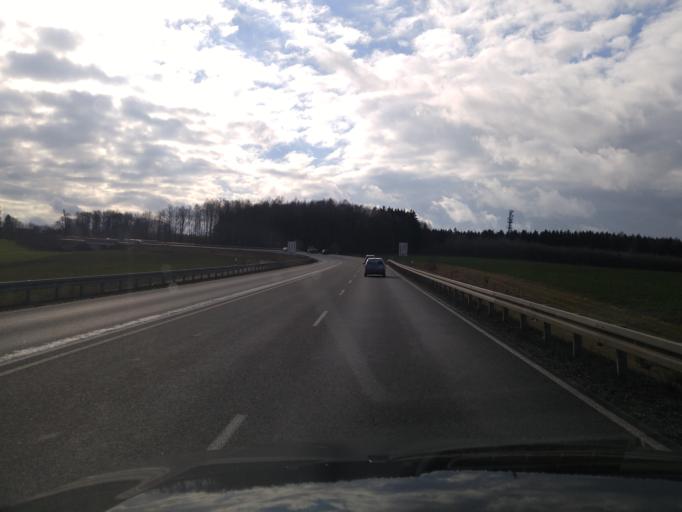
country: DE
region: Saxony
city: Hirschfeld
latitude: 50.6439
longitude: 12.4411
